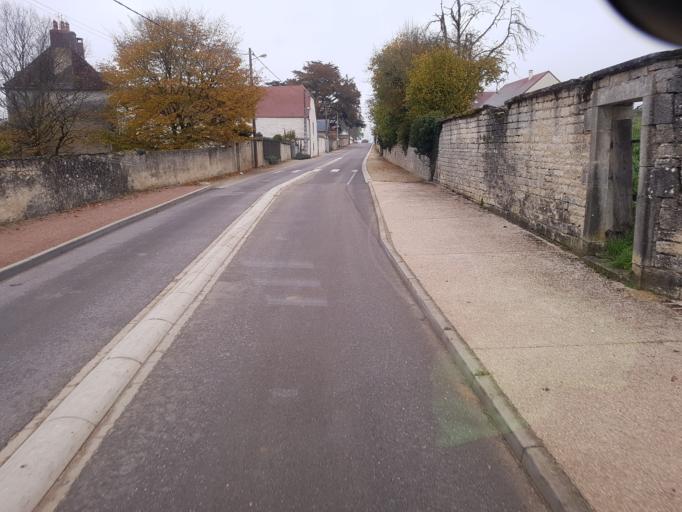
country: FR
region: Bourgogne
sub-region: Departement de la Cote-d'Or
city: Arc-sur-Tille
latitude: 47.3862
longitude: 5.1900
